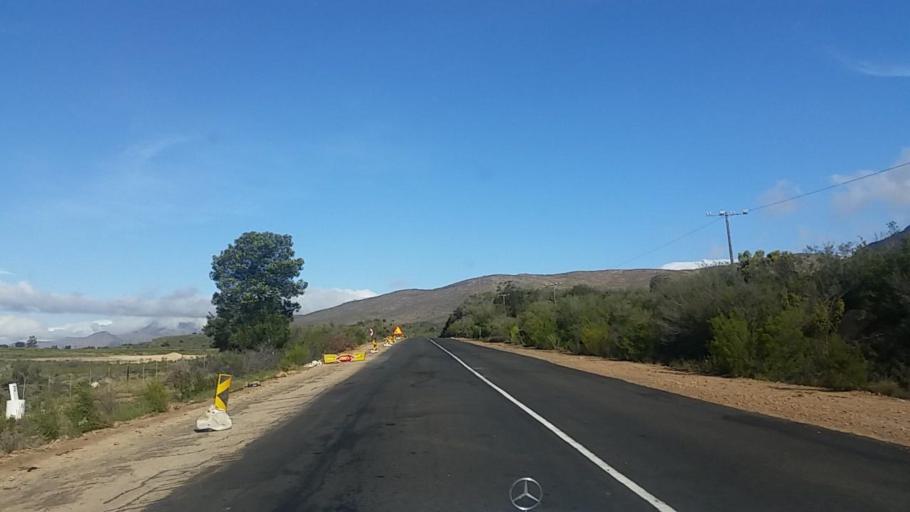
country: ZA
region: Western Cape
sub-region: Eden District Municipality
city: George
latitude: -33.8235
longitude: 22.3847
